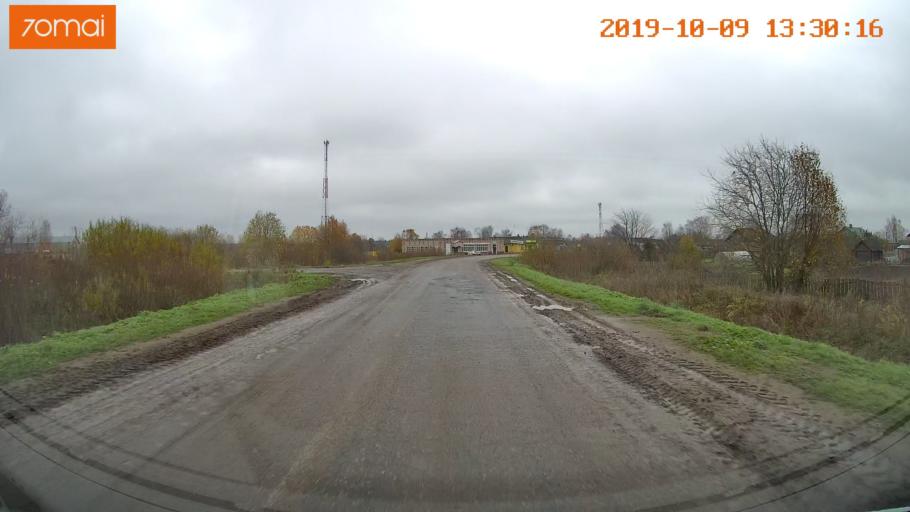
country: RU
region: Jaroslavl
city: Lyubim
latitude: 58.3215
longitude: 41.0045
